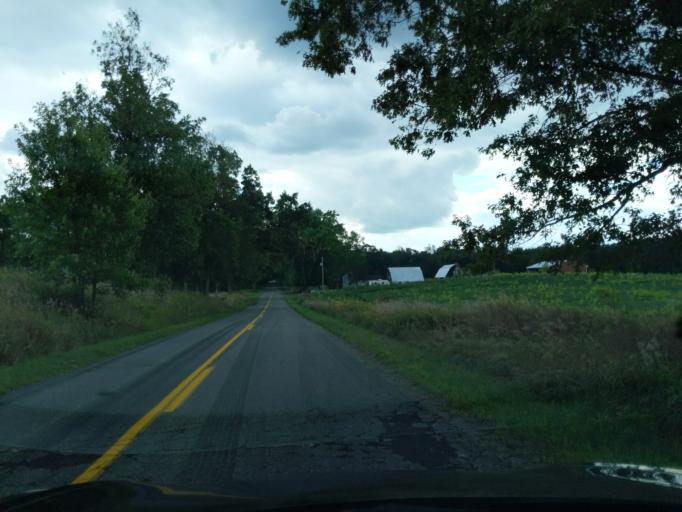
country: US
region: Michigan
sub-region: Eaton County
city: Eaton Rapids
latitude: 42.4183
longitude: -84.5808
